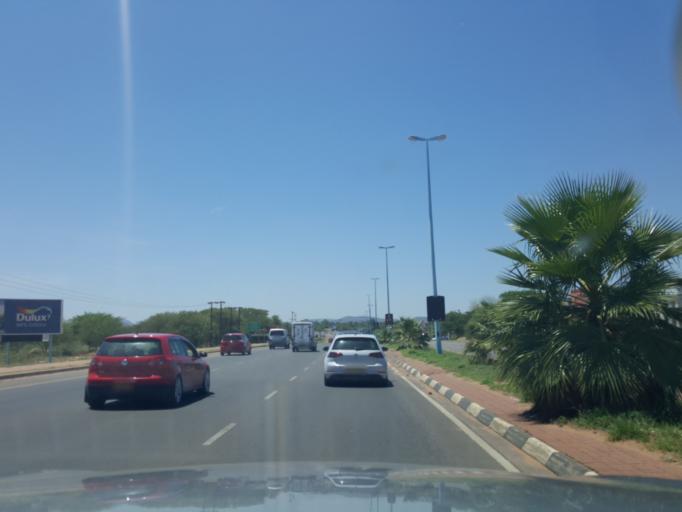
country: BW
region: Kweneng
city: Mogoditshane
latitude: -24.6382
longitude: 25.8795
